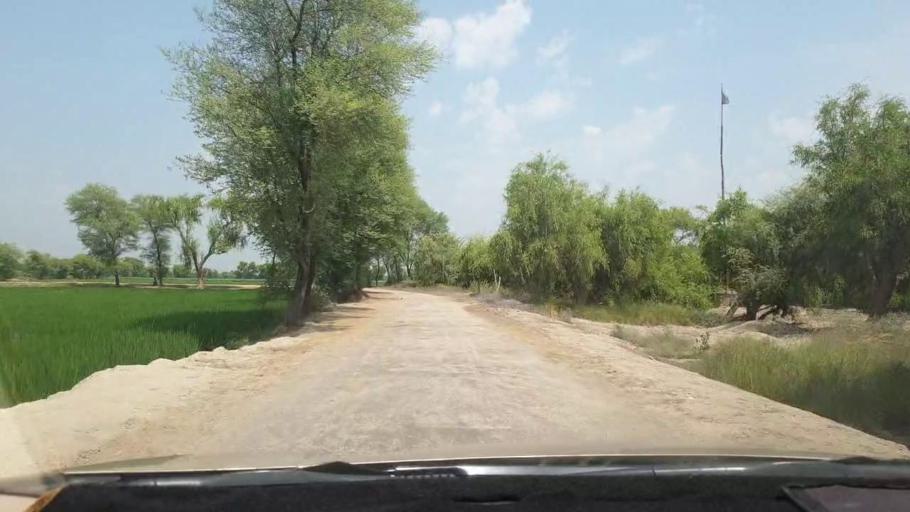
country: PK
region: Sindh
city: Naudero
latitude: 27.7355
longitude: 68.3510
